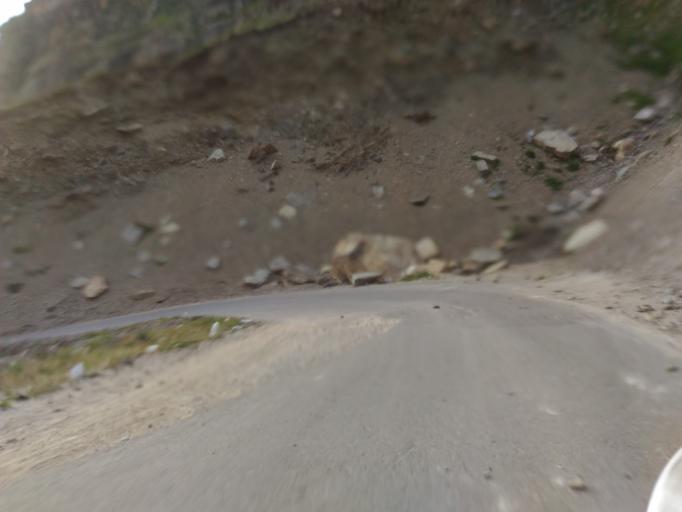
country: IN
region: Himachal Pradesh
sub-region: Kulu
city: Manali
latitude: 32.4363
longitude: 77.1834
